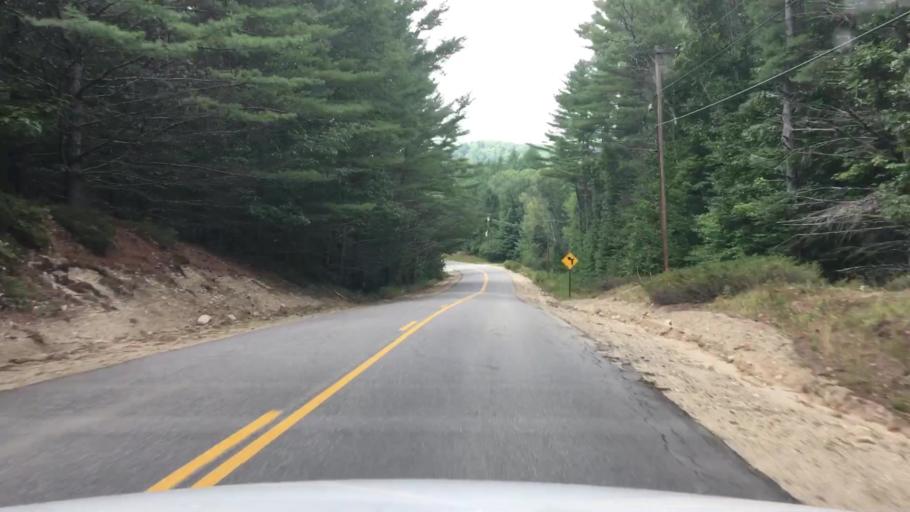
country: US
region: Maine
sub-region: Oxford County
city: Rumford
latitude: 44.5458
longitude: -70.6795
